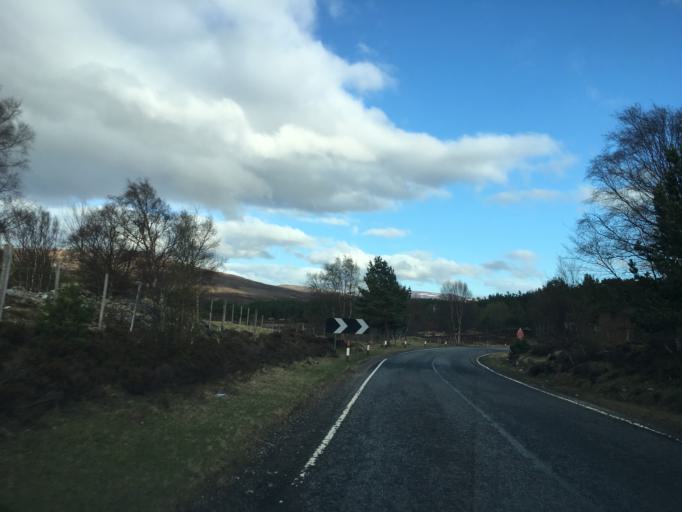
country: GB
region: Scotland
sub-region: Highland
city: Kingussie
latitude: 56.9907
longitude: -4.2490
